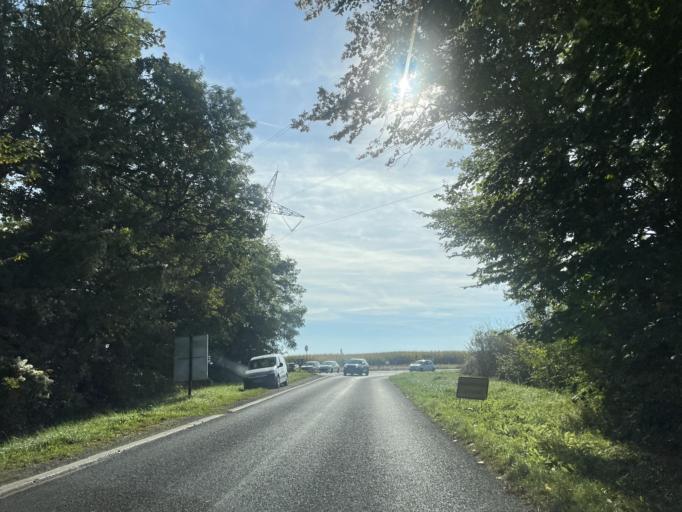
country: FR
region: Ile-de-France
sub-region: Departement de Seine-et-Marne
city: Saint-Jean-les-Deux-Jumeaux
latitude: 48.9482
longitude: 2.9920
